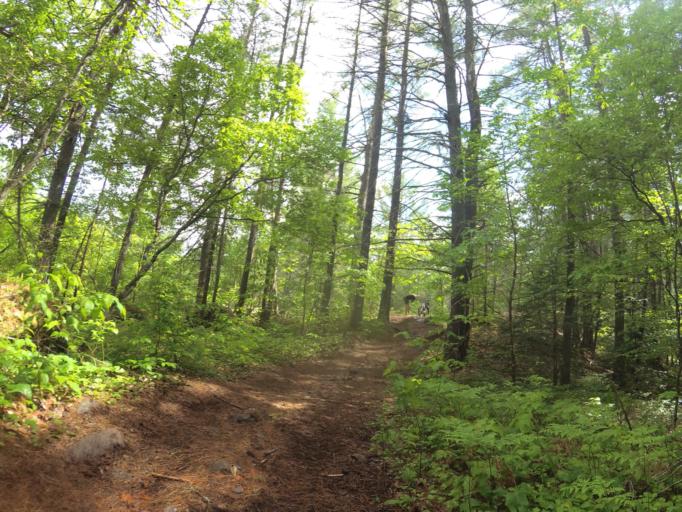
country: CA
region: Ontario
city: Renfrew
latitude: 45.1263
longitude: -76.8418
